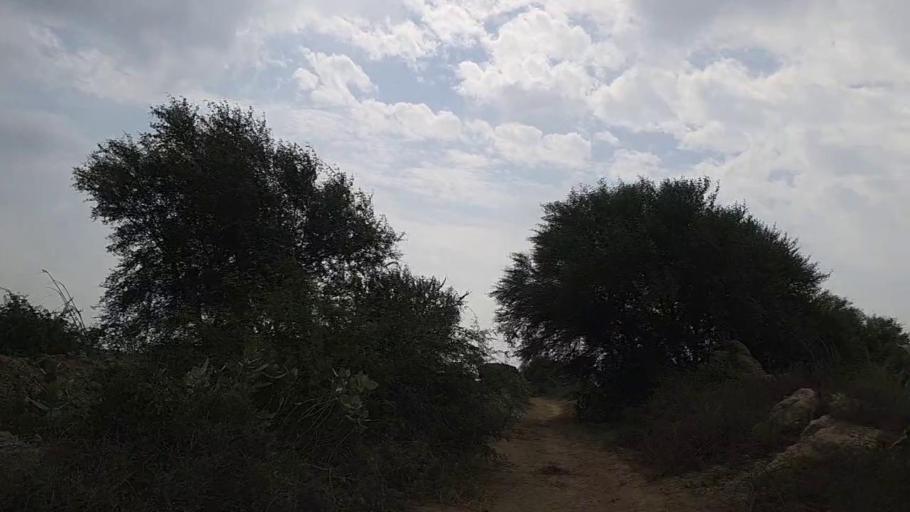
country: PK
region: Sindh
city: Mirpur Batoro
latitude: 24.6171
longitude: 68.1361
